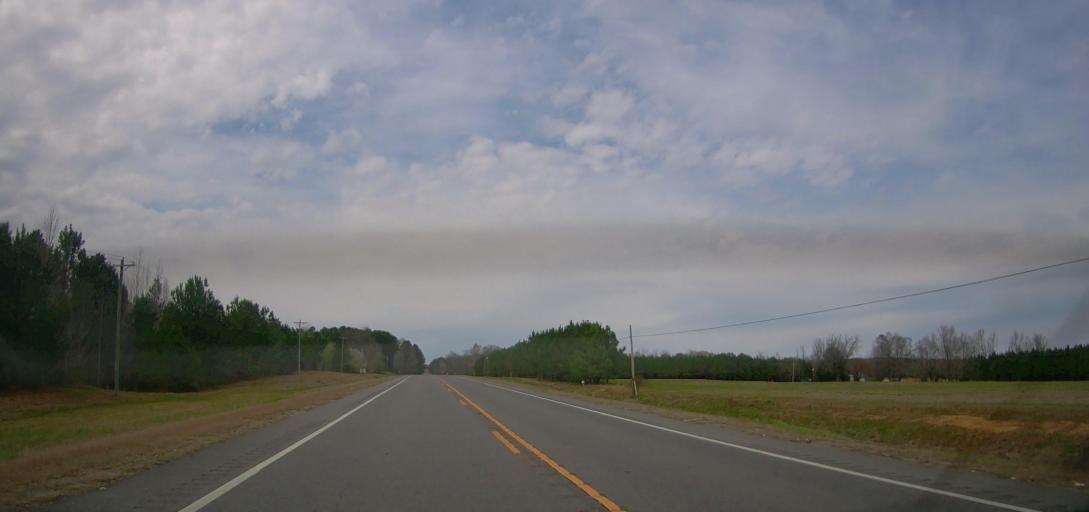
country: US
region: Alabama
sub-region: Marion County
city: Guin
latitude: 34.0047
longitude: -87.9329
